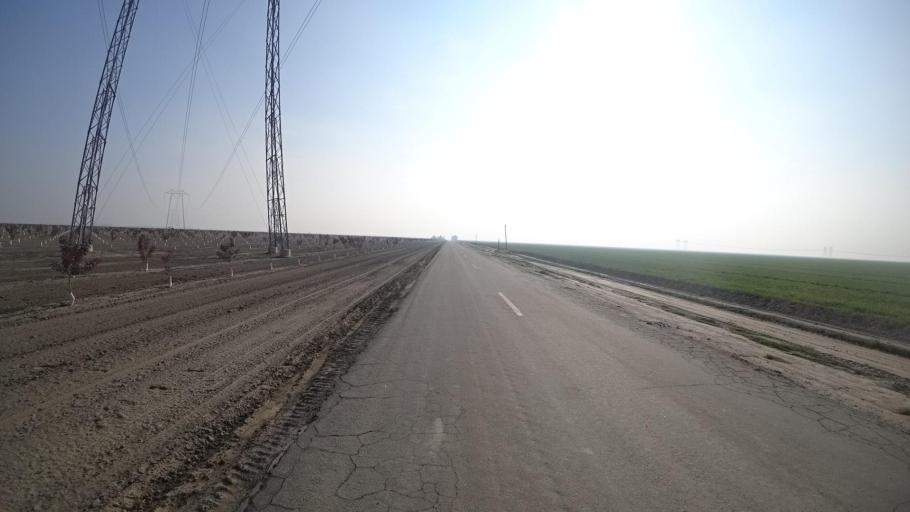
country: US
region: California
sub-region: Kern County
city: Greenfield
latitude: 35.1711
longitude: -119.0393
